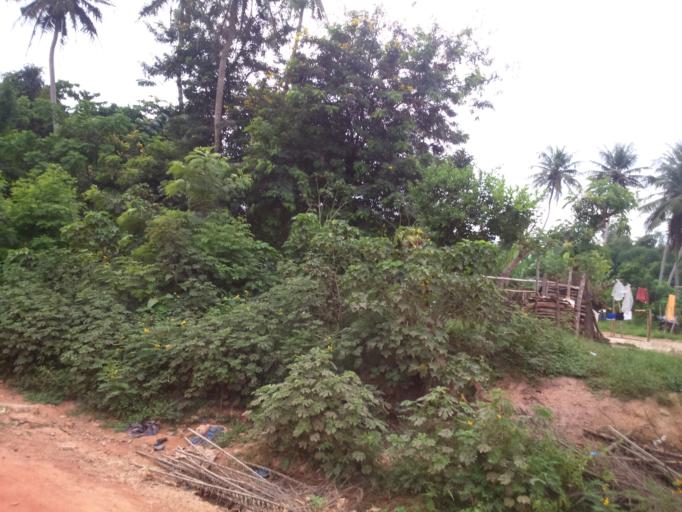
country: CI
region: Agneby
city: Agboville
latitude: 6.0291
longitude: -4.1304
